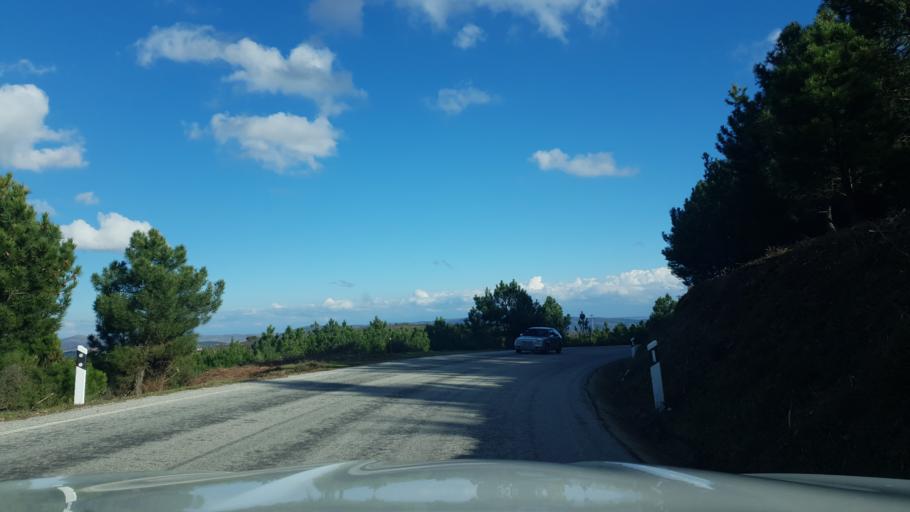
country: PT
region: Braganca
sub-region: Torre de Moncorvo
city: Torre de Moncorvo
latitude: 41.1825
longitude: -6.9416
